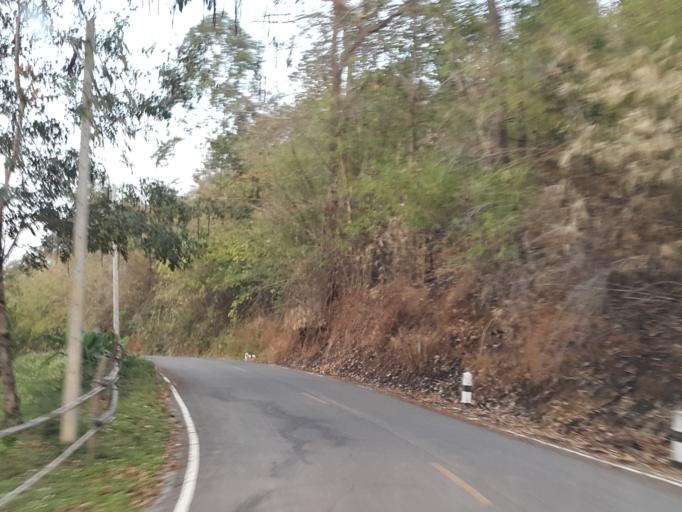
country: TH
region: Lampang
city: Mueang Pan
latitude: 18.8248
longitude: 99.4559
